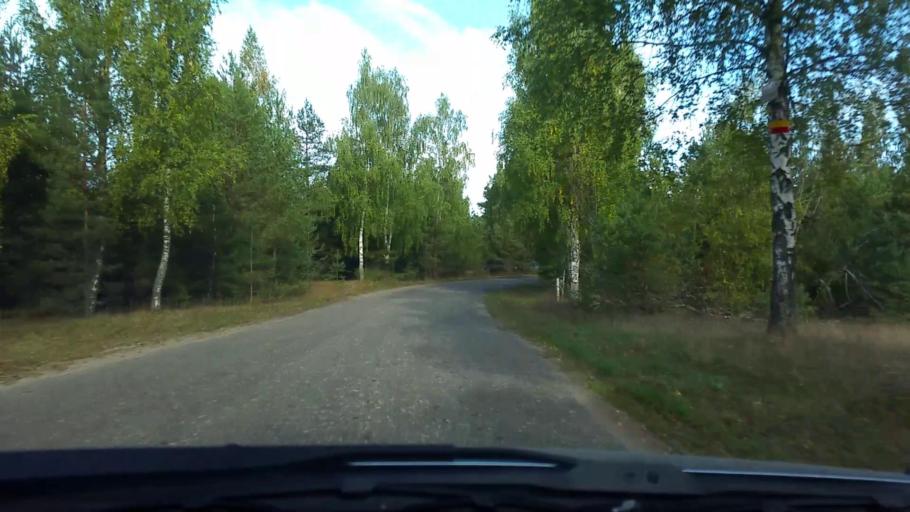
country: LV
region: Adazi
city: Adazi
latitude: 57.1140
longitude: 24.3623
